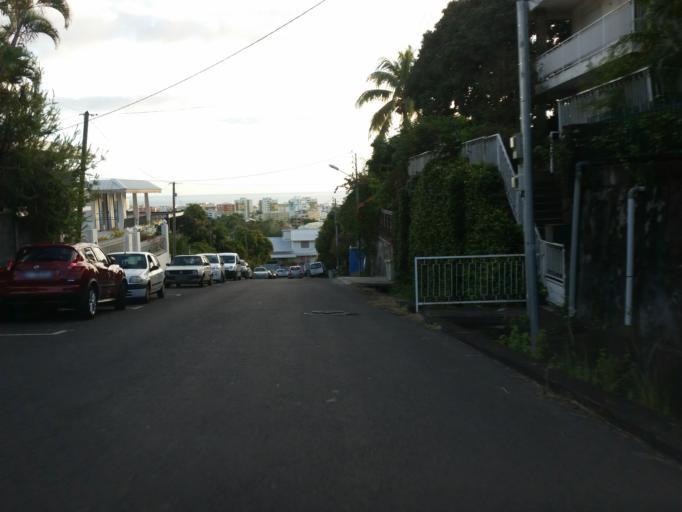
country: RE
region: Reunion
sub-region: Reunion
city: Saint-Denis
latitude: -20.8999
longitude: 55.4564
